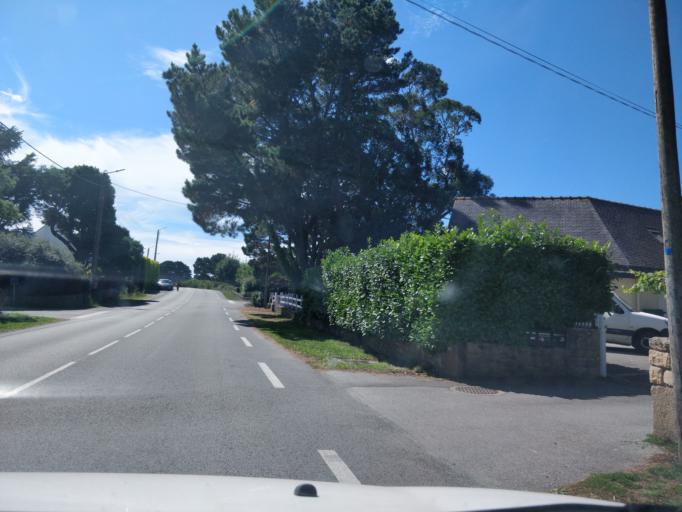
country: FR
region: Brittany
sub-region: Departement du Morbihan
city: Saint-Philibert
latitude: 47.5754
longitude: -3.0004
